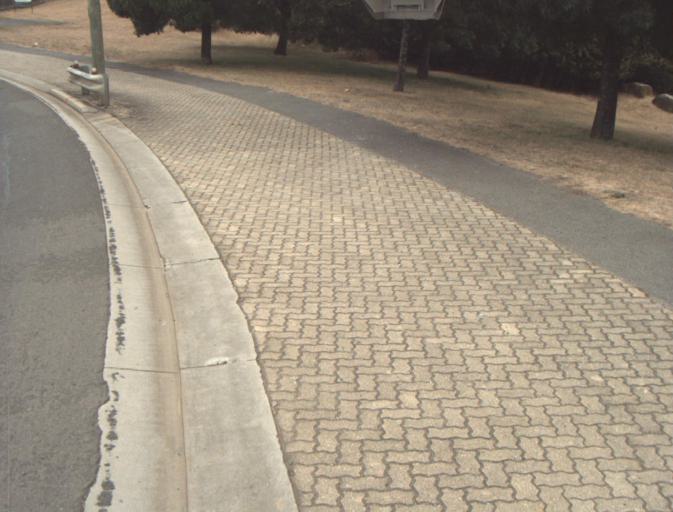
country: AU
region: Tasmania
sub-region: Launceston
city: Newstead
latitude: -41.4387
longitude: 147.1805
